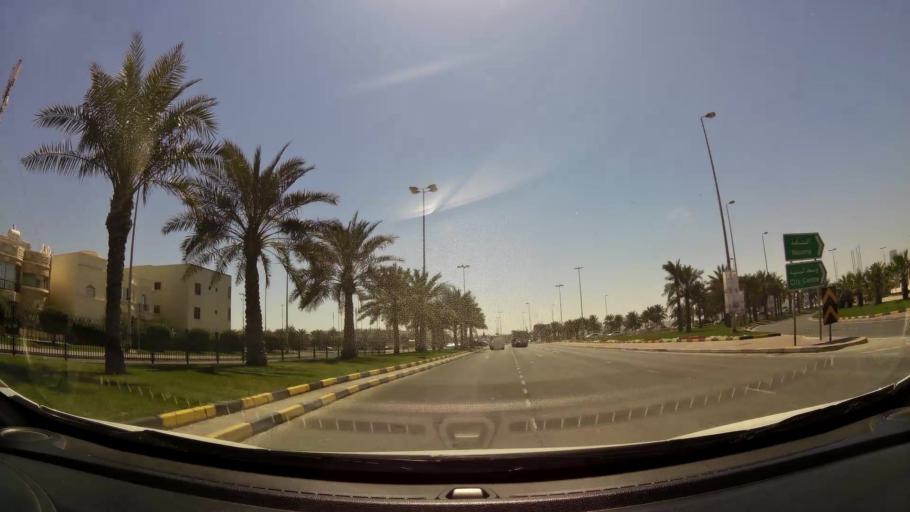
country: BH
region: Muharraq
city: Al Muharraq
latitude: 26.2616
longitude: 50.6032
